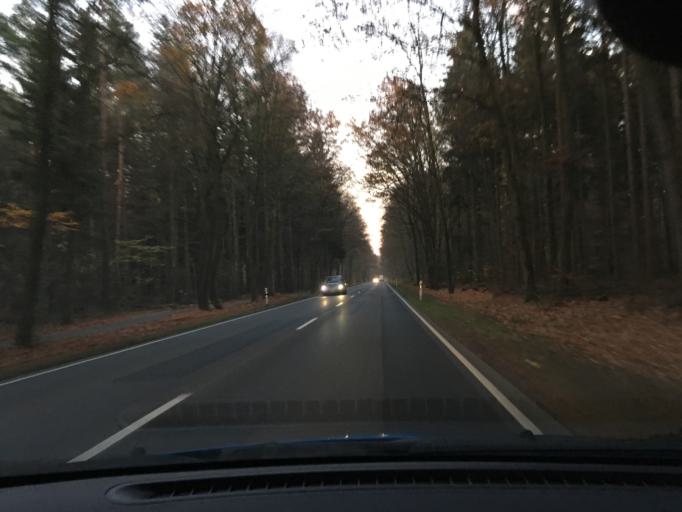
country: DE
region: Lower Saxony
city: Uelzen
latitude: 52.9813
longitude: 10.5273
